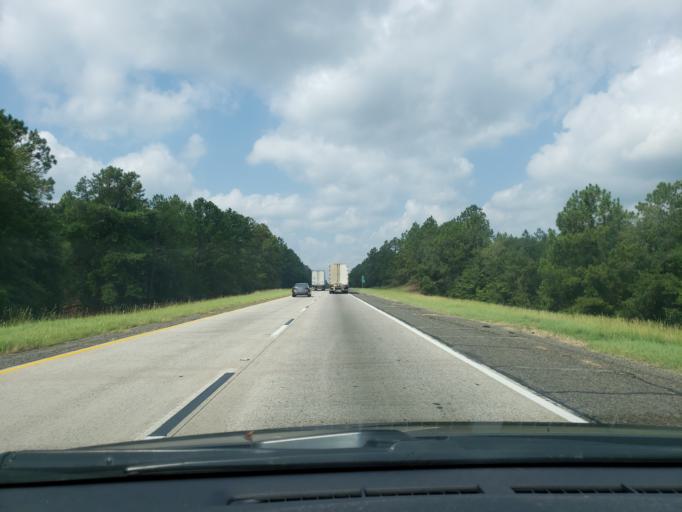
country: US
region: Georgia
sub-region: Treutlen County
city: Soperton
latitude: 32.4294
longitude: -82.5286
